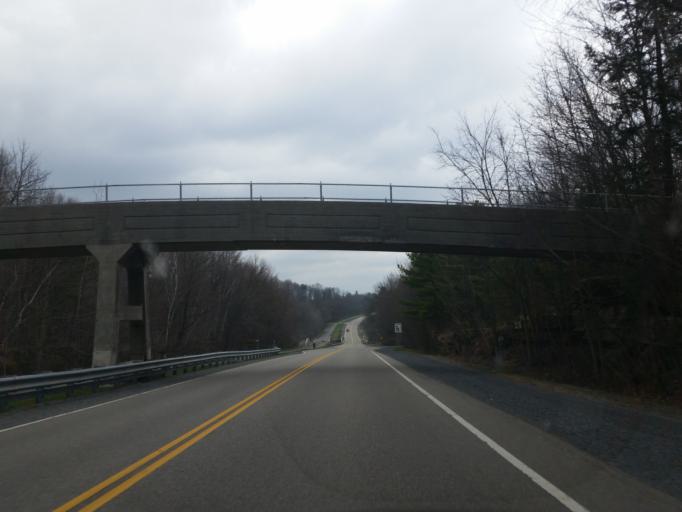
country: CA
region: Ontario
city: Brockville
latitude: 44.5006
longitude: -75.8083
